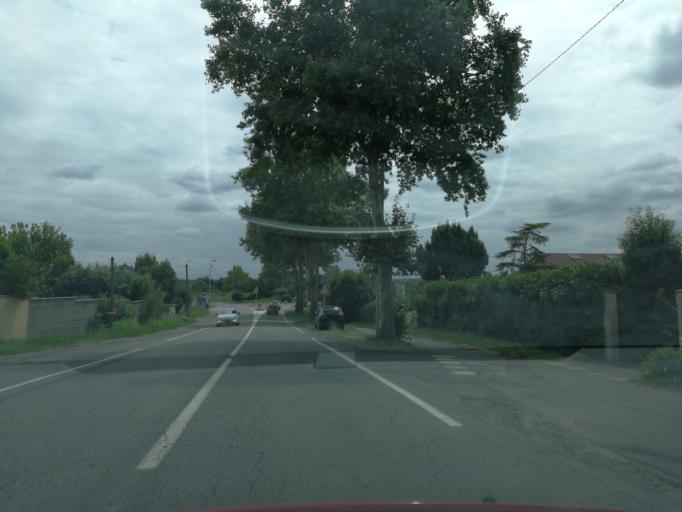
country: FR
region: Midi-Pyrenees
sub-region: Departement de la Haute-Garonne
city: Balma
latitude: 43.5805
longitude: 1.5109
